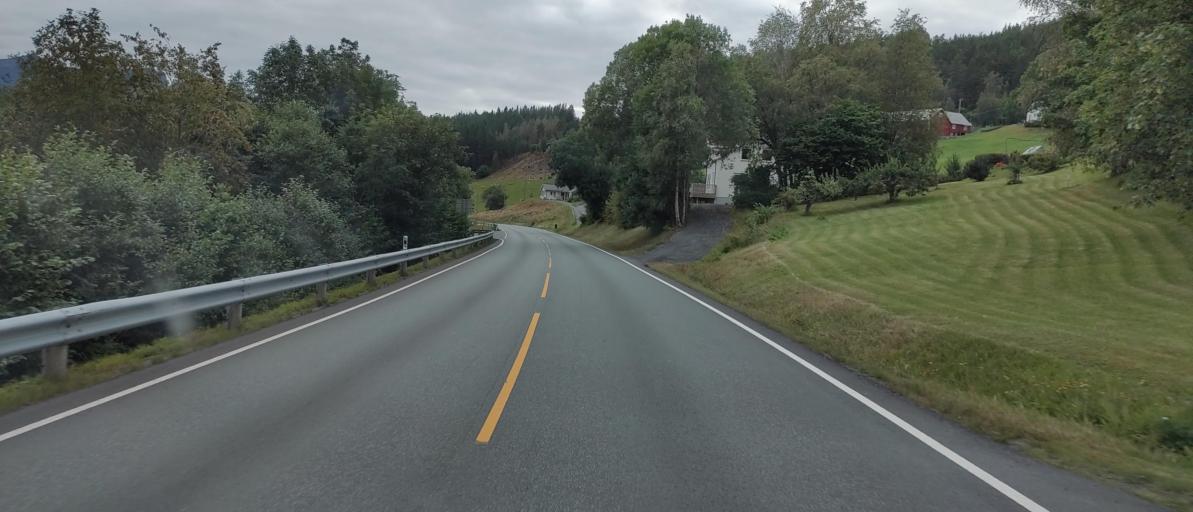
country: NO
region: More og Romsdal
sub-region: Rauma
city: Andalsnes
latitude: 62.5804
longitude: 7.5602
